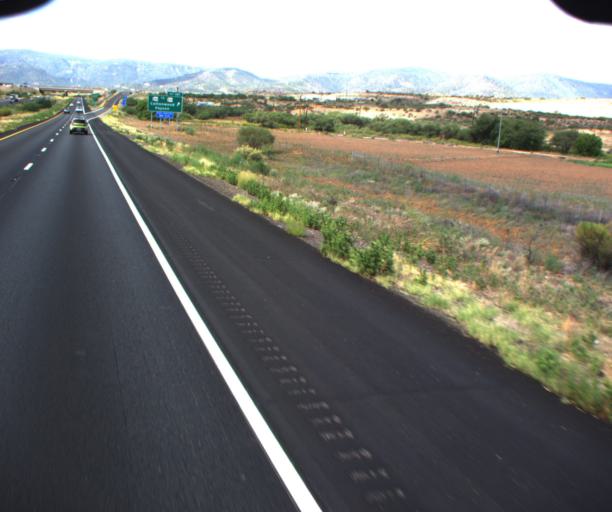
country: US
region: Arizona
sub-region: Yavapai County
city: Camp Verde
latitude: 34.5850
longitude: -111.8806
